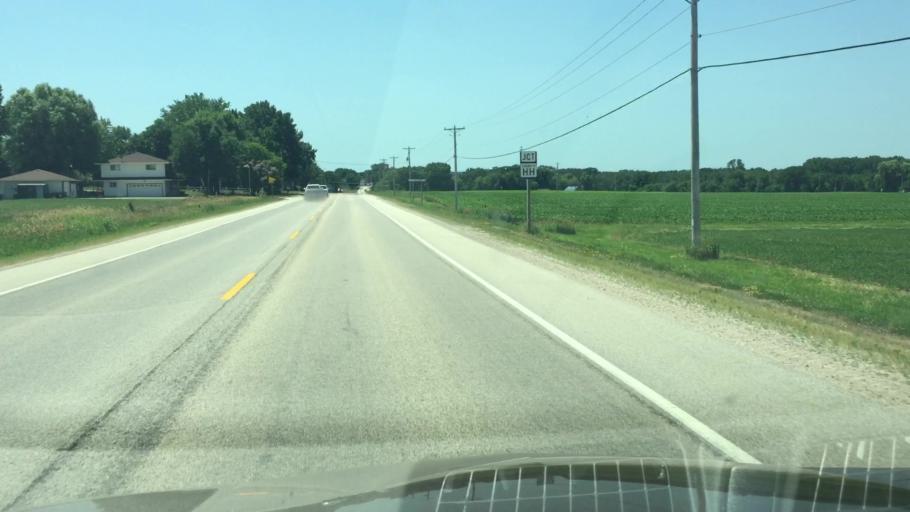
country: US
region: Wisconsin
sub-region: Fond du Lac County
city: Saint Peter
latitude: 43.9236
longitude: -88.3077
